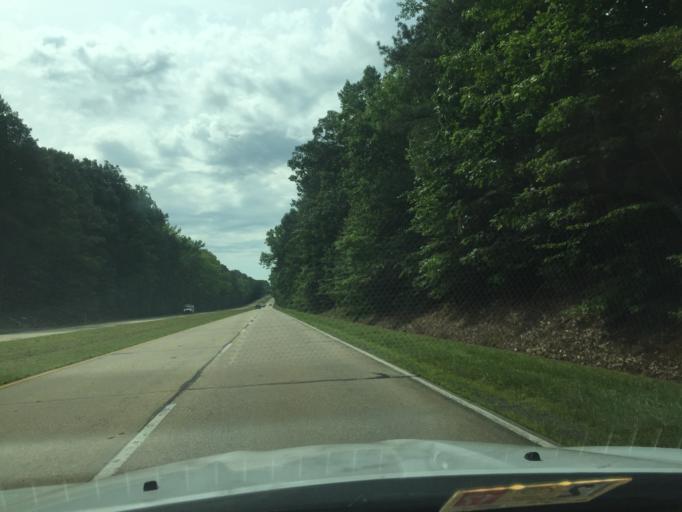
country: US
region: Virginia
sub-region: Charles City County
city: Charles City
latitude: 37.4699
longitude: -77.1138
